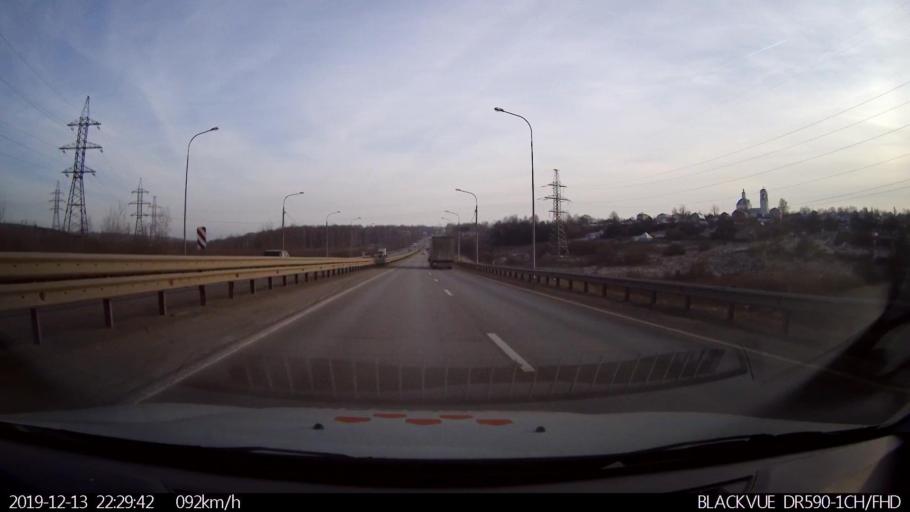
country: RU
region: Nizjnij Novgorod
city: Afonino
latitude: 56.2348
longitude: 44.0532
